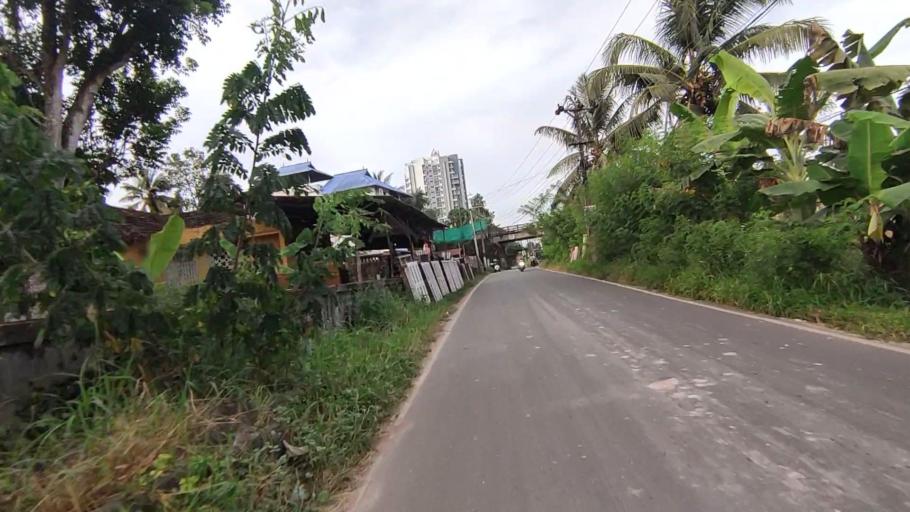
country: IN
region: Kerala
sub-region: Kottayam
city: Kottayam
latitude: 9.5954
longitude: 76.5021
